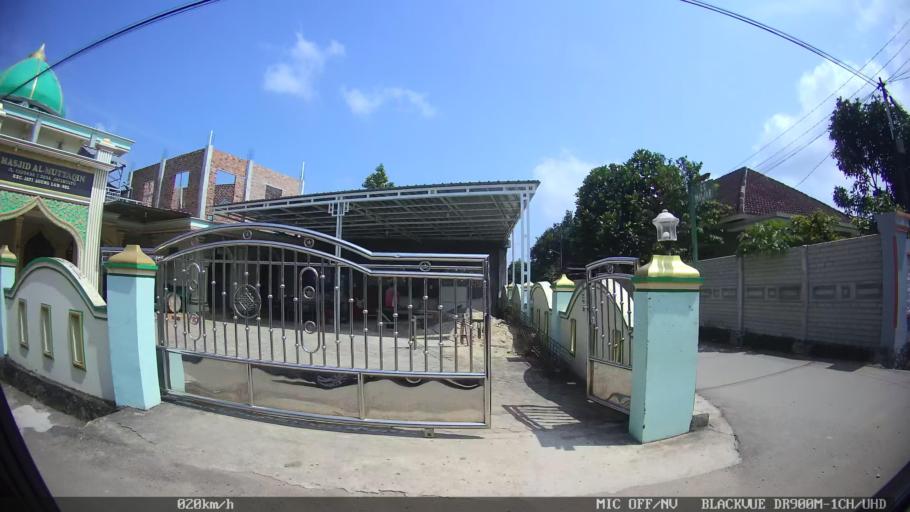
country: ID
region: Lampung
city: Kedaton
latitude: -5.3456
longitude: 105.2901
